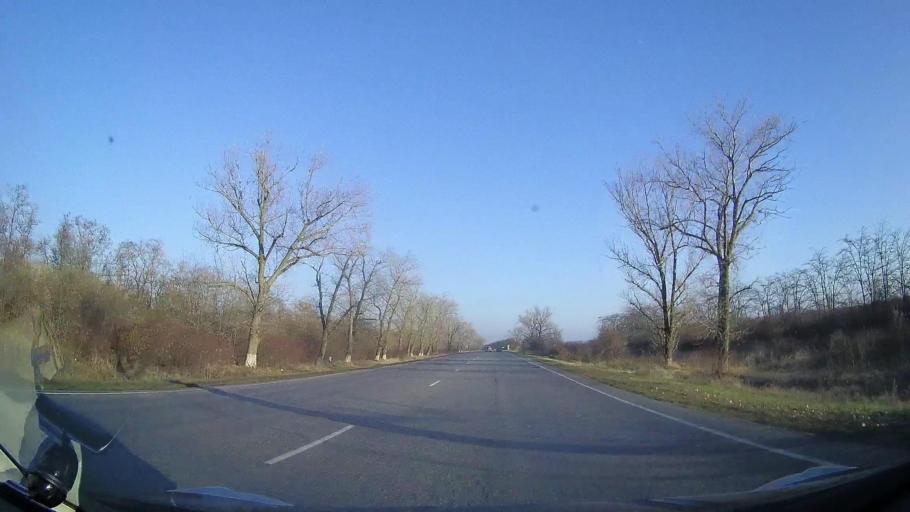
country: RU
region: Rostov
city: Kirovskaya
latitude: 47.0081
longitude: 39.9484
